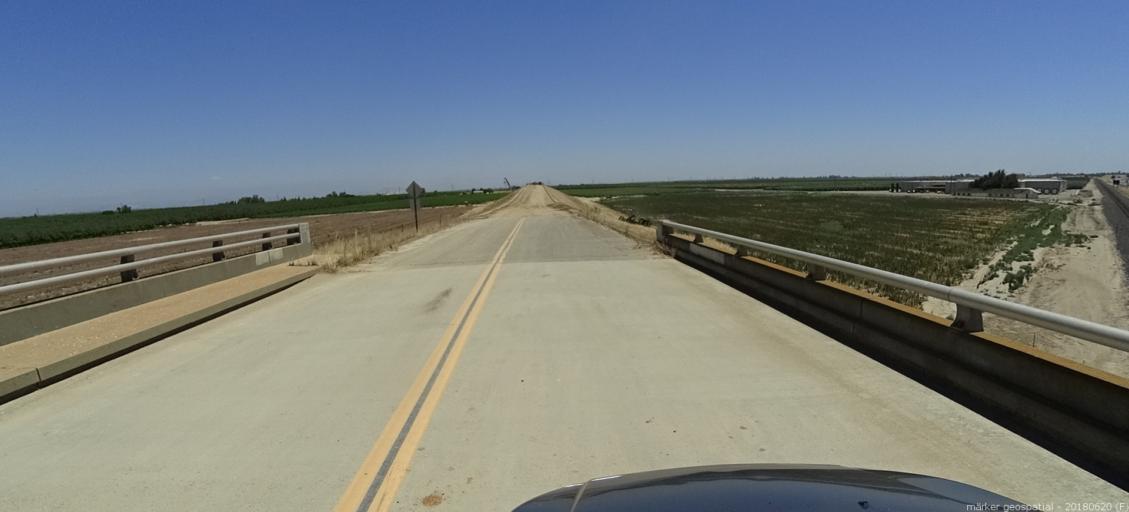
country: US
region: California
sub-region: Fresno County
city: Biola
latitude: 36.8658
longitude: -119.9601
